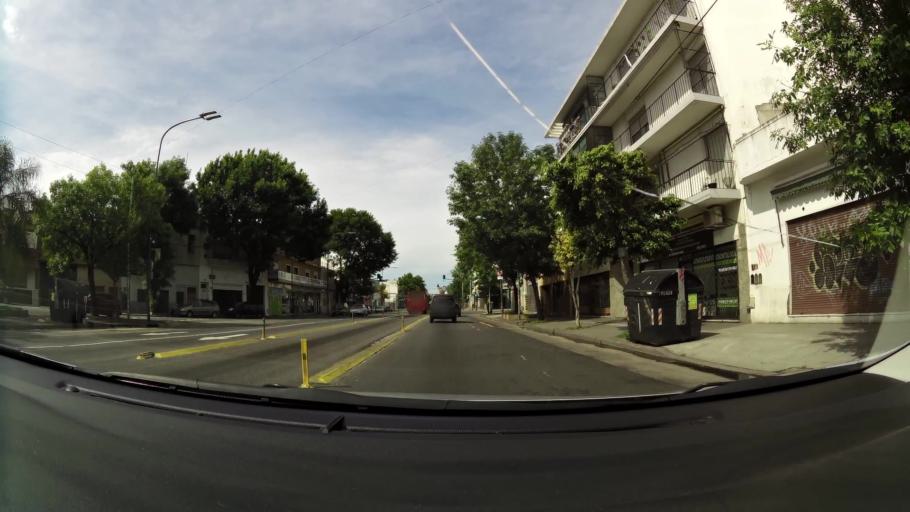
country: AR
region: Buenos Aires F.D.
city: Buenos Aires
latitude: -34.6409
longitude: -58.4204
